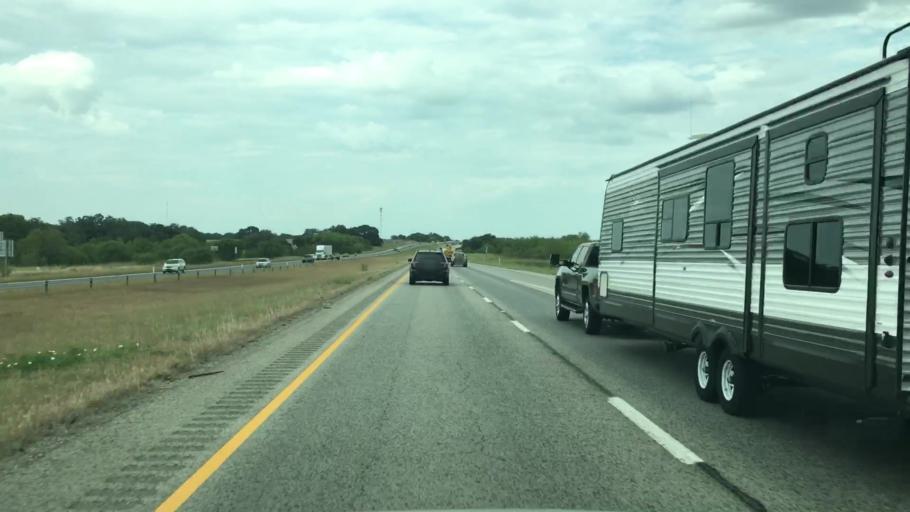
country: US
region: Texas
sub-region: Atascosa County
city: Pleasanton
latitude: 29.1108
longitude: -98.4320
